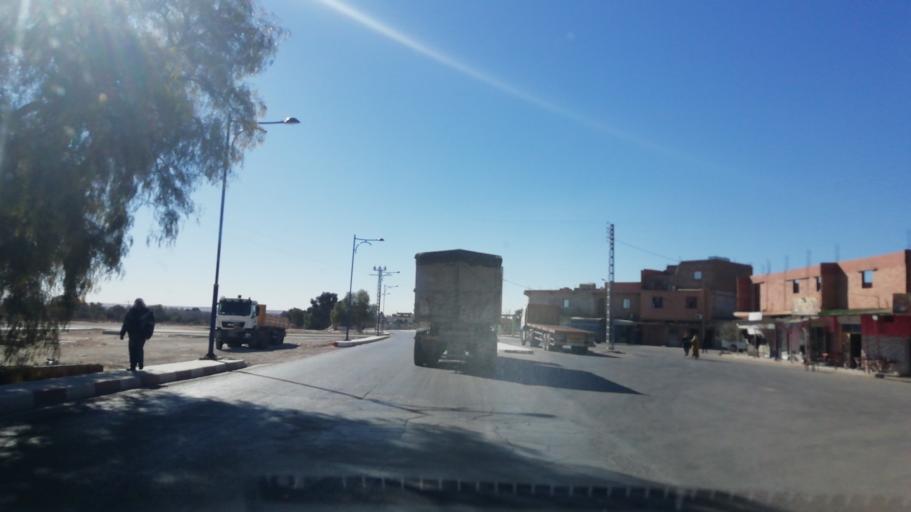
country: DZ
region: Saida
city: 'Ain el Hadjar
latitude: 34.1515
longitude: 0.0697
